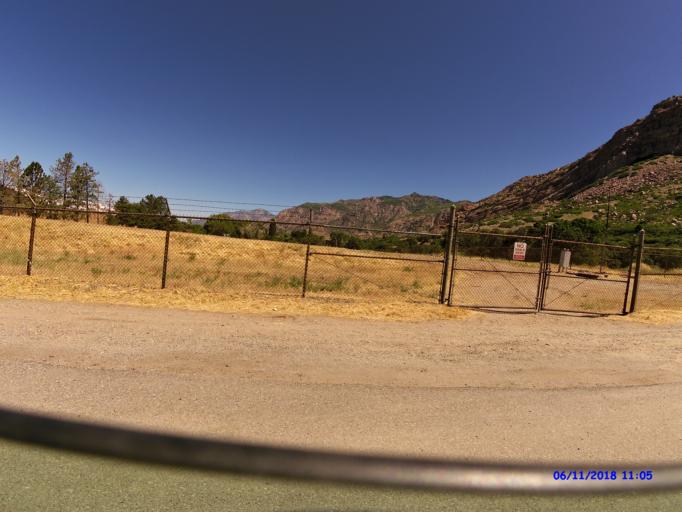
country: US
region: Utah
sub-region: Weber County
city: Ogden
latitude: 41.2191
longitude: -111.9307
